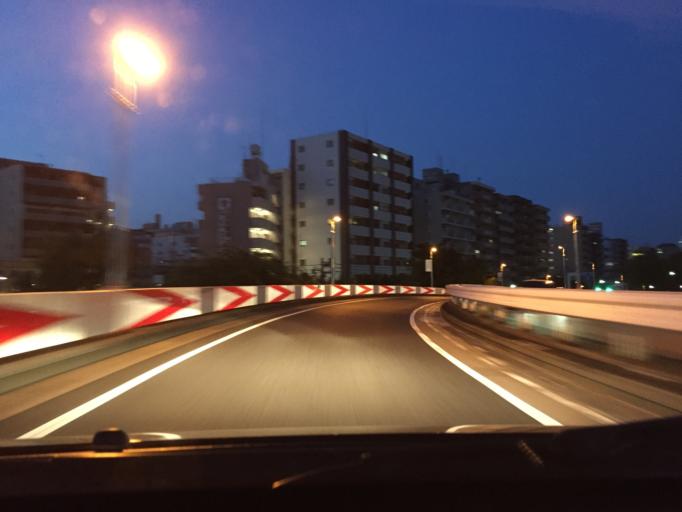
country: JP
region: Kanagawa
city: Yokohama
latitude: 35.4365
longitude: 139.6232
